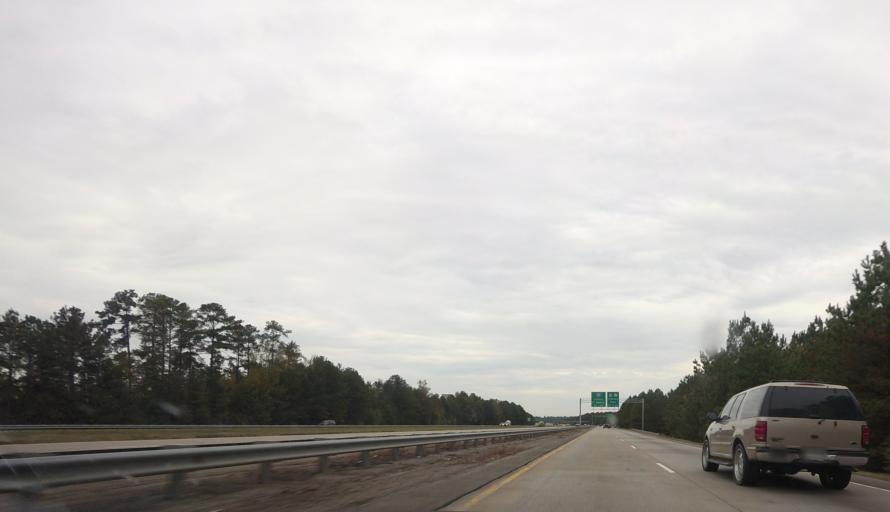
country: US
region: Alabama
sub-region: Russell County
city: Phenix City
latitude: 32.5510
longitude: -84.9410
